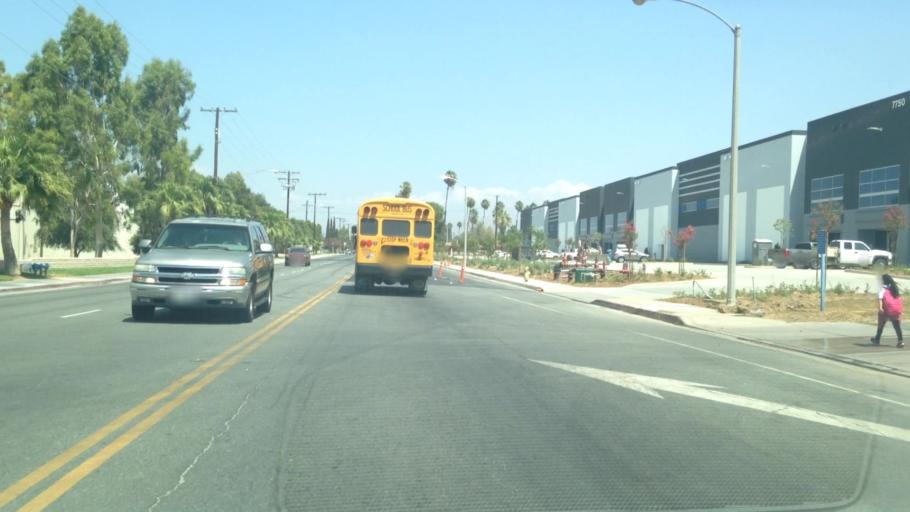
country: US
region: California
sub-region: Riverside County
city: Riverside
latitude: 33.9254
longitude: -117.4056
